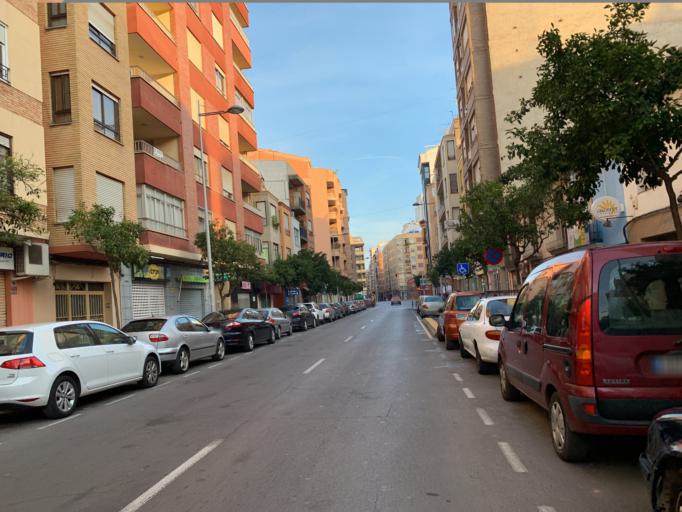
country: ES
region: Valencia
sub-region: Provincia de Castello
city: Castello de la Plana
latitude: 39.9903
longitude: -0.0419
